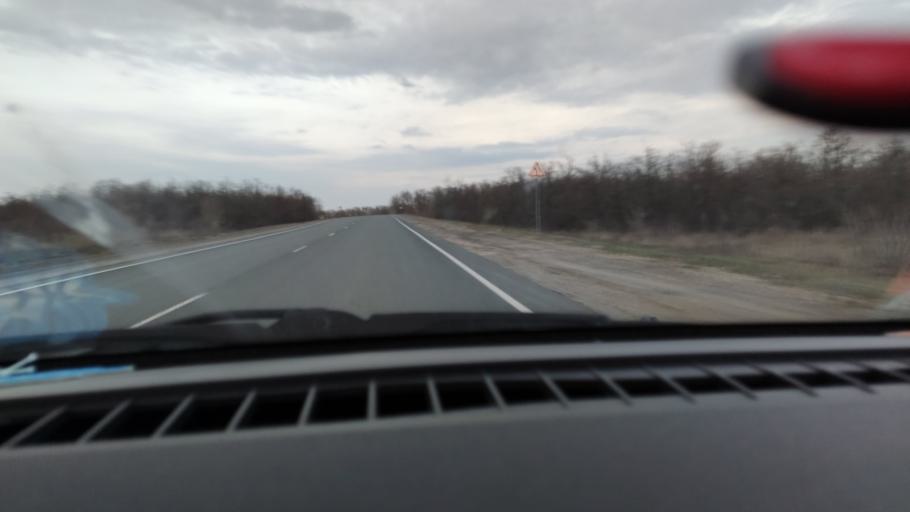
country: RU
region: Saratov
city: Sinodskoye
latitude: 51.9361
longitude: 46.5914
